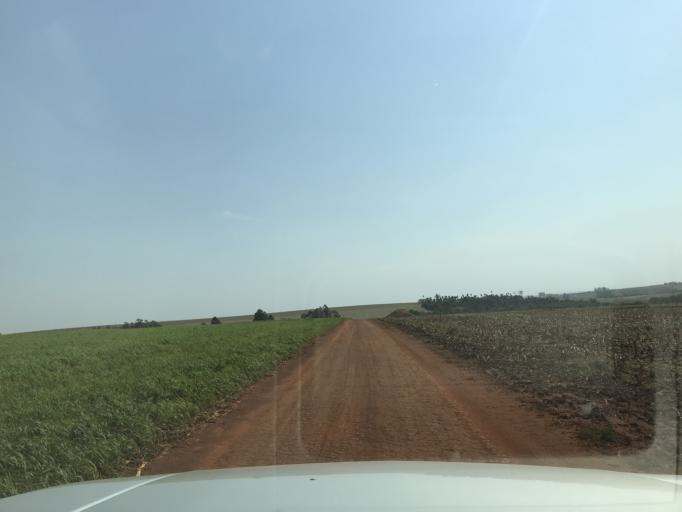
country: BR
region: Parana
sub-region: Palotina
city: Palotina
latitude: -24.2281
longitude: -53.7385
